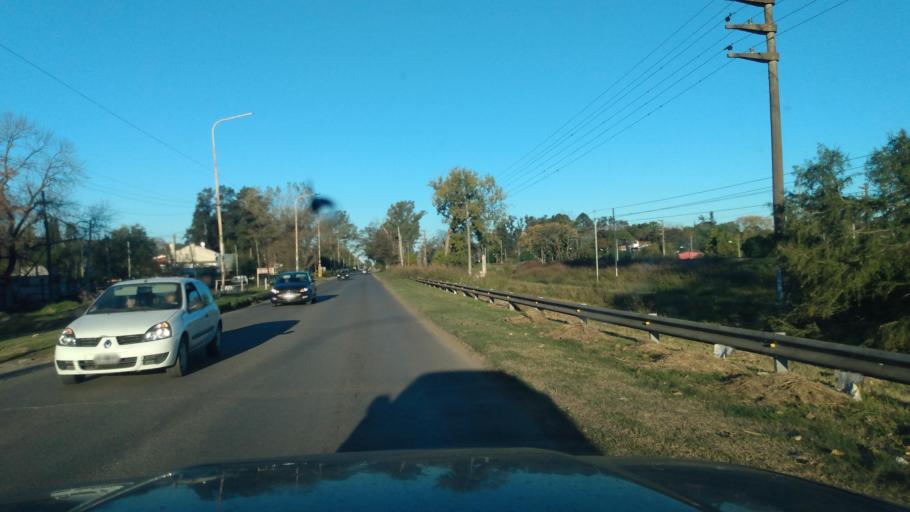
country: AR
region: Buenos Aires
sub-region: Partido de General Rodriguez
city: General Rodriguez
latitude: -34.6360
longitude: -58.8405
